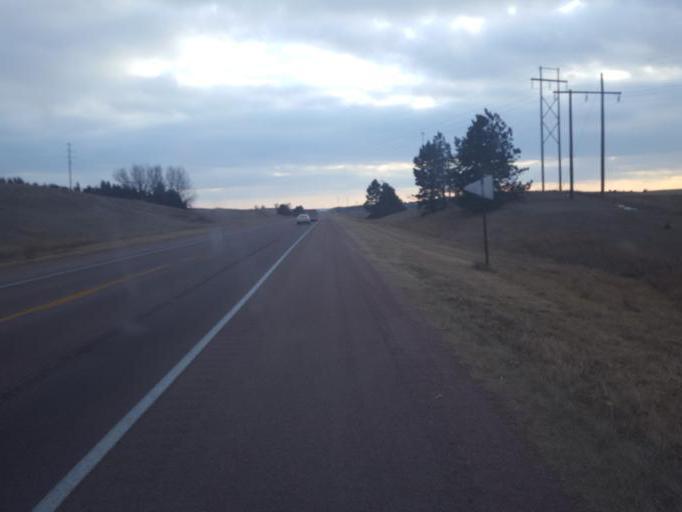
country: US
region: South Dakota
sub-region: Yankton County
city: Yankton
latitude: 42.7354
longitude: -97.4070
